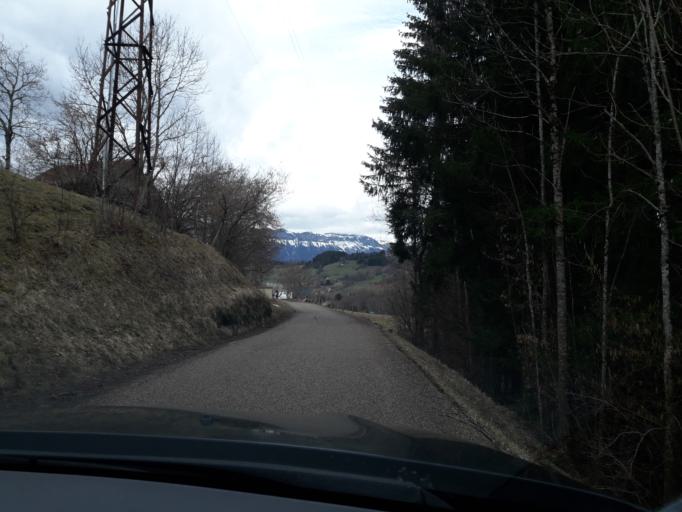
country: FR
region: Rhone-Alpes
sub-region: Departement de l'Isere
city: Le Champ-pres-Froges
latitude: 45.2403
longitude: 5.9679
